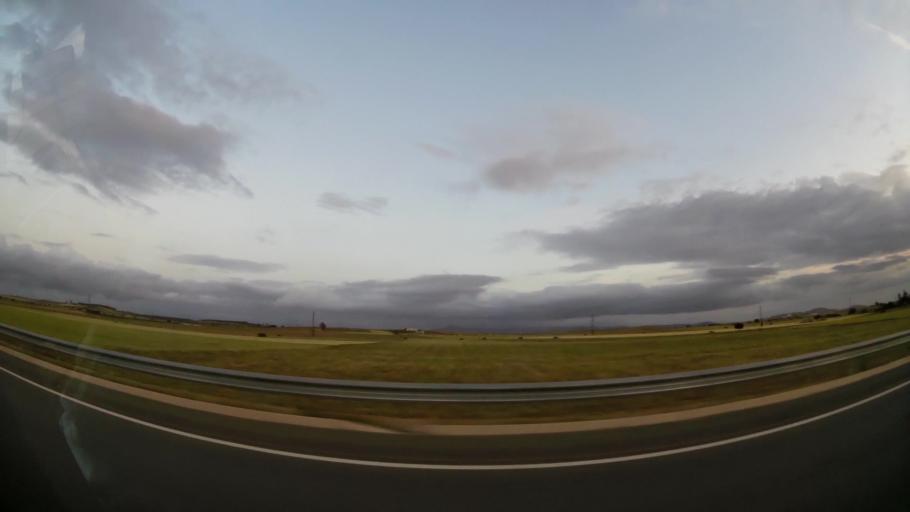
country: MA
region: Oriental
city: El Aioun
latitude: 34.6261
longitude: -2.5207
